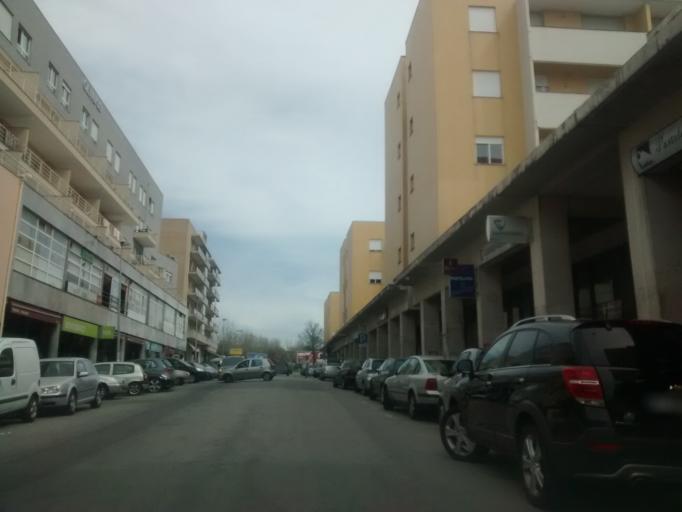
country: PT
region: Braga
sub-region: Braga
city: Braga
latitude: 41.5574
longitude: -8.3992
